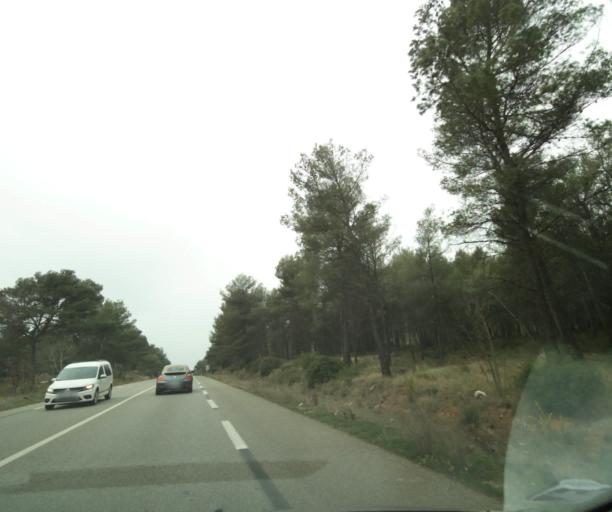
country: FR
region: Provence-Alpes-Cote d'Azur
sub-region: Departement des Bouches-du-Rhone
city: Chateauneuf-le-Rouge
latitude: 43.4898
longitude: 5.5643
